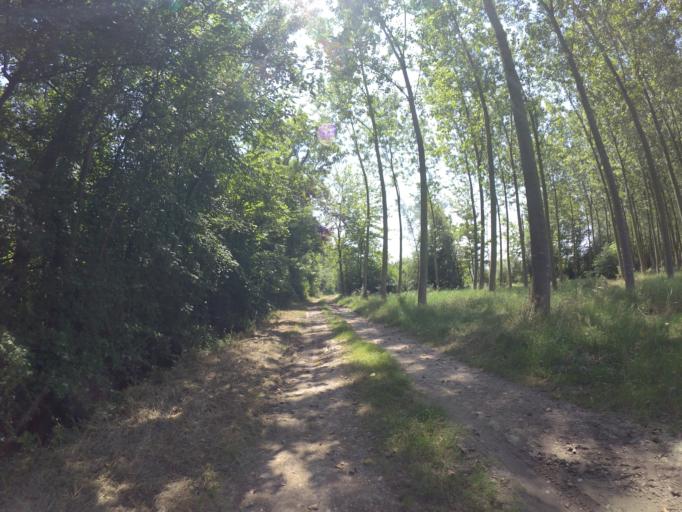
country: IT
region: Friuli Venezia Giulia
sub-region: Provincia di Udine
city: Rivignano
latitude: 45.8985
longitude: 13.0394
